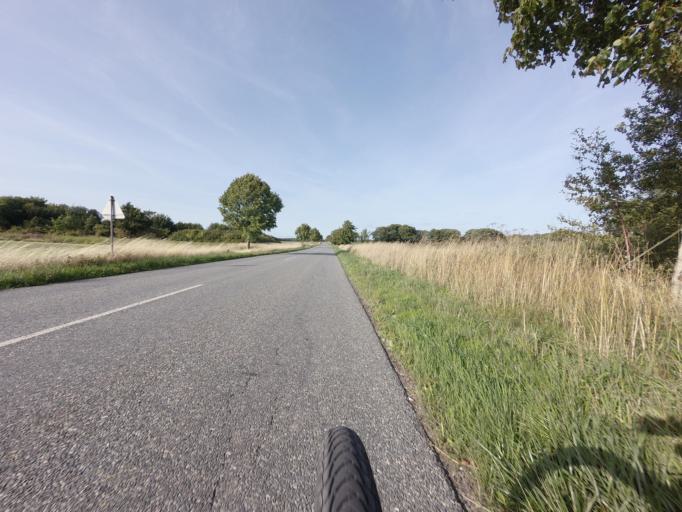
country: DK
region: Zealand
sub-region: Faxe Kommune
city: Fakse Ladeplads
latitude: 55.2395
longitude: 12.2158
